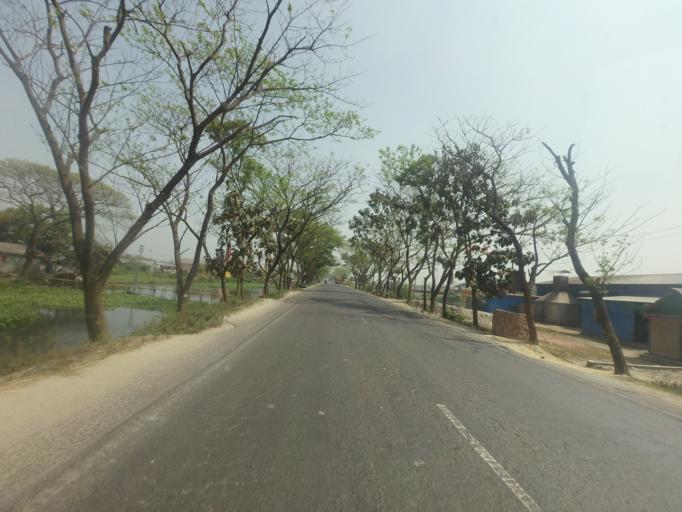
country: BD
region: Dhaka
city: Bhairab Bazar
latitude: 24.0428
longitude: 91.0515
